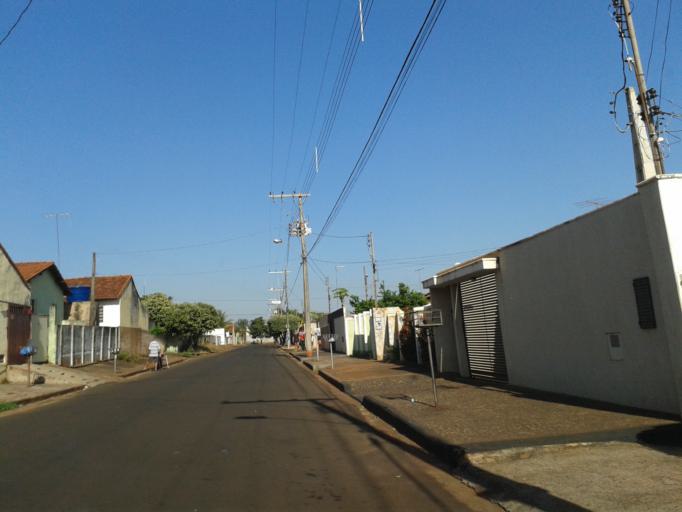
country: BR
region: Minas Gerais
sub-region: Ituiutaba
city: Ituiutaba
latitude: -18.9693
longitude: -49.4859
